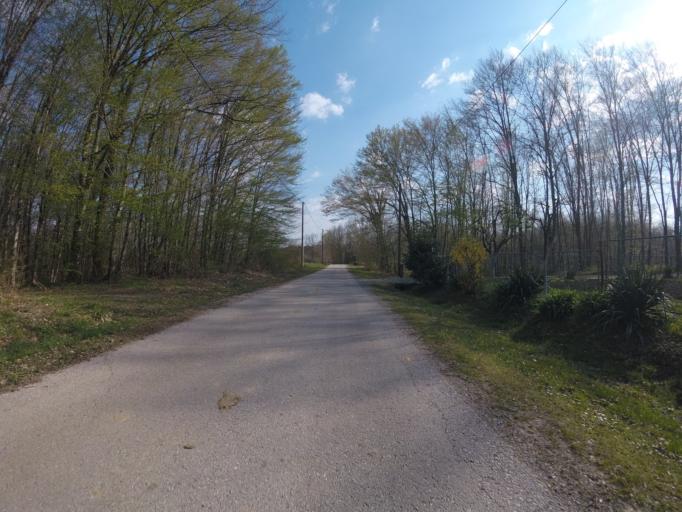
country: HR
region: Sisacko-Moslavacka
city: Glina
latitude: 45.4888
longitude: 16.0021
